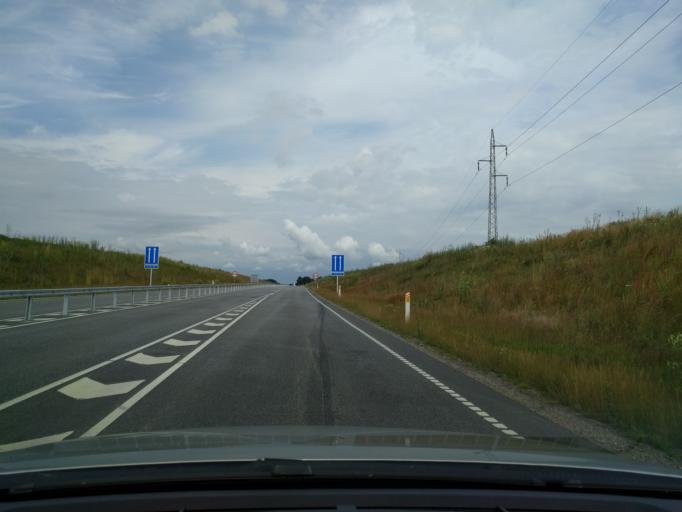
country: DK
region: Zealand
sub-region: Naestved Kommune
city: Fensmark
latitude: 55.2582
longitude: 11.8032
